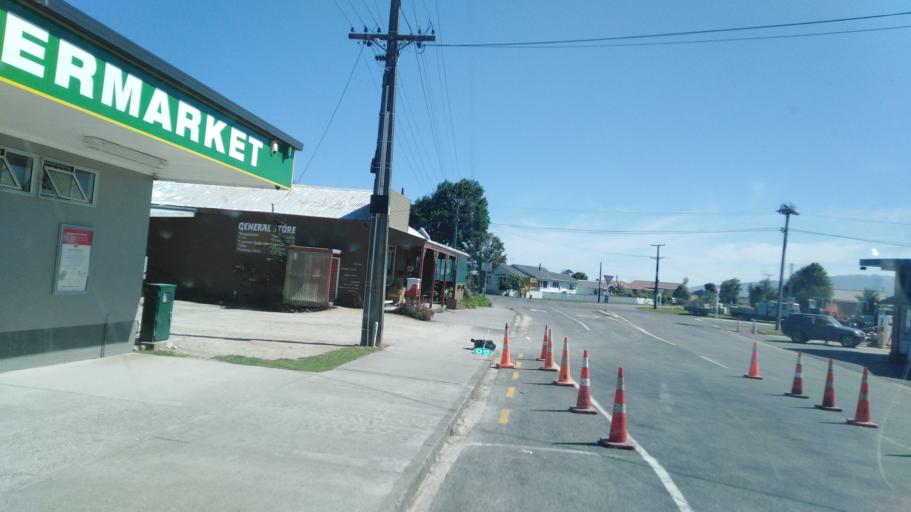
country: NZ
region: West Coast
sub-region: Buller District
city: Westport
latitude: -41.2515
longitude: 172.1286
